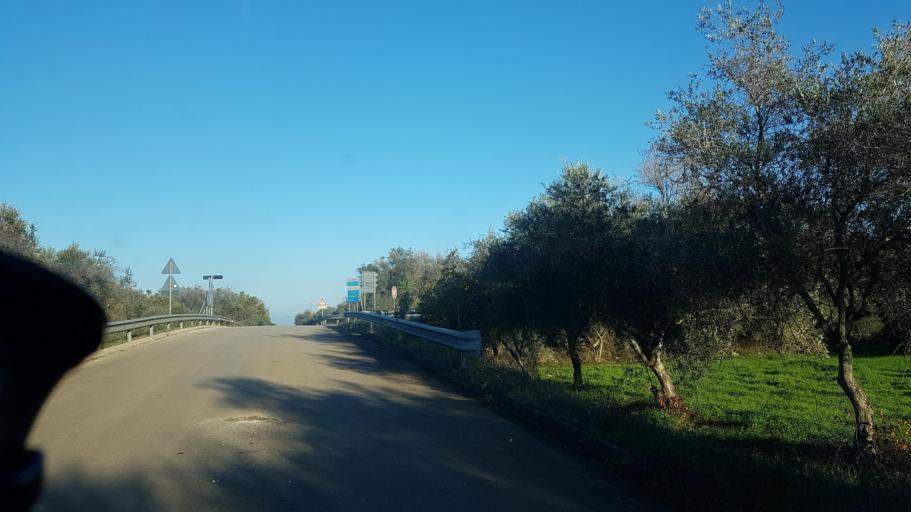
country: IT
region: Apulia
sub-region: Provincia di Brindisi
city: Latiano
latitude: 40.5621
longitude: 17.7319
